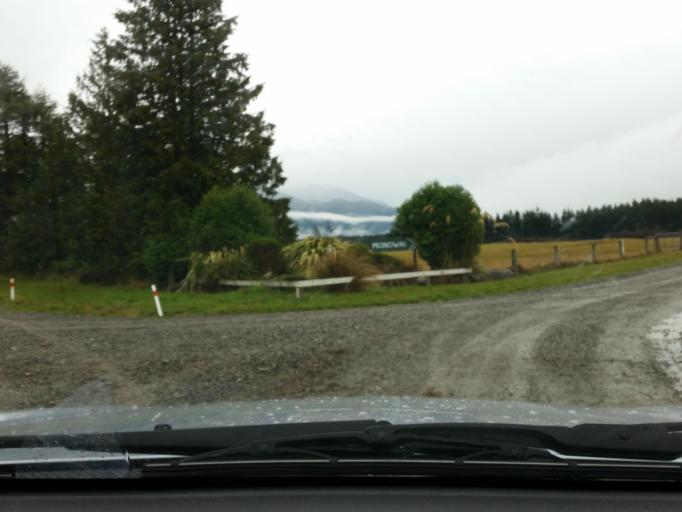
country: NZ
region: Southland
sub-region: Southland District
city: Te Anau
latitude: -45.7825
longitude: 167.6082
